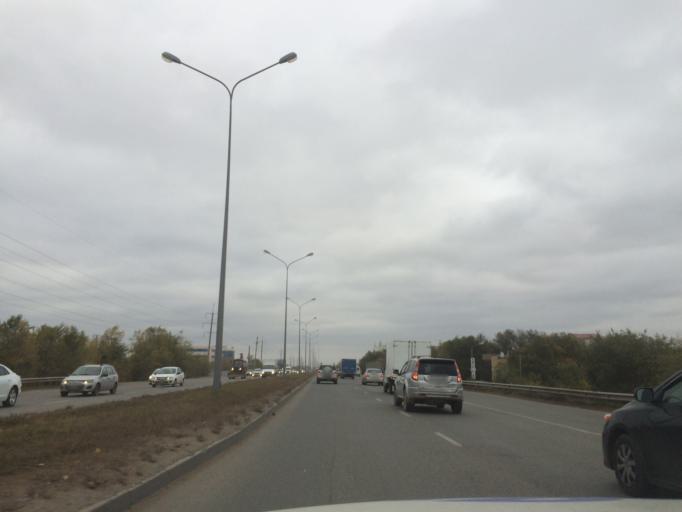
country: KZ
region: Astana Qalasy
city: Astana
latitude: 51.1913
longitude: 71.4603
